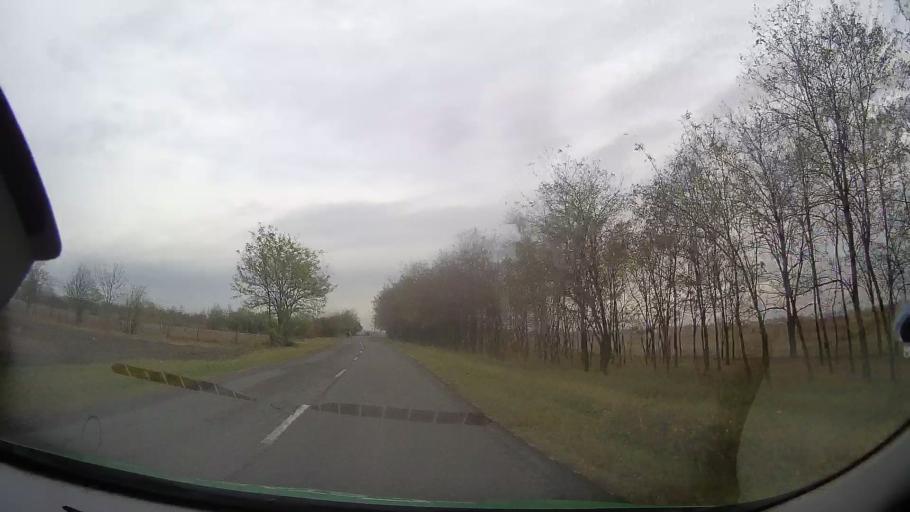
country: RO
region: Prahova
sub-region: Comuna Berceni
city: Berceni
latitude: 44.9390
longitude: 26.1117
